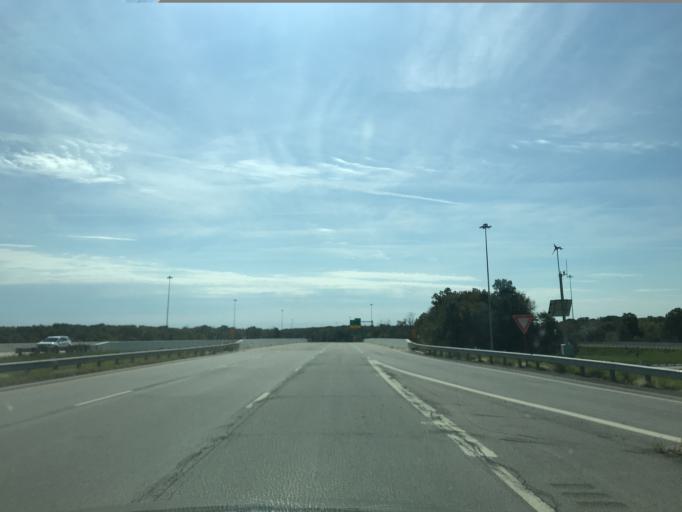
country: US
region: Ohio
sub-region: Ashtabula County
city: Ashtabula
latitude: 41.8291
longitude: -80.7656
